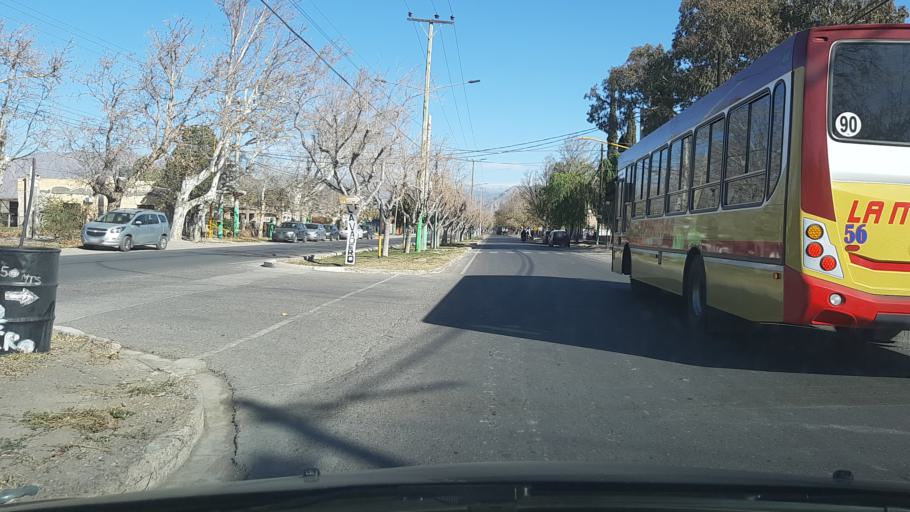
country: AR
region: San Juan
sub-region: Departamento de Rivadavia
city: Rivadavia
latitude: -31.5260
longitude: -68.6308
